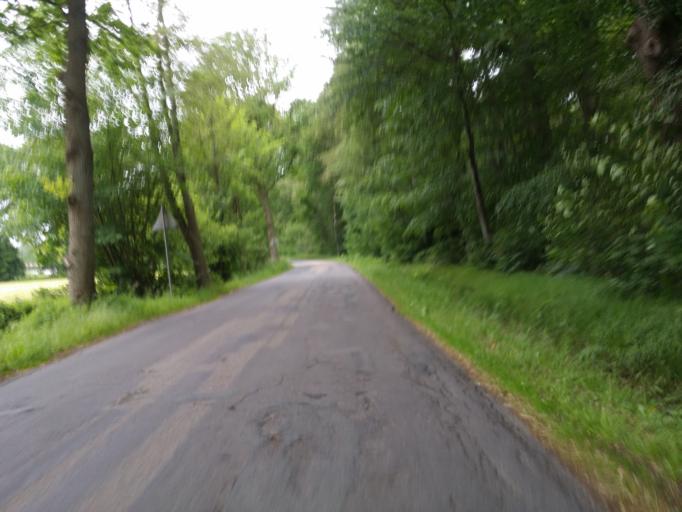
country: DE
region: Lower Saxony
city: Rastede
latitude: 53.2388
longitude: 8.2173
